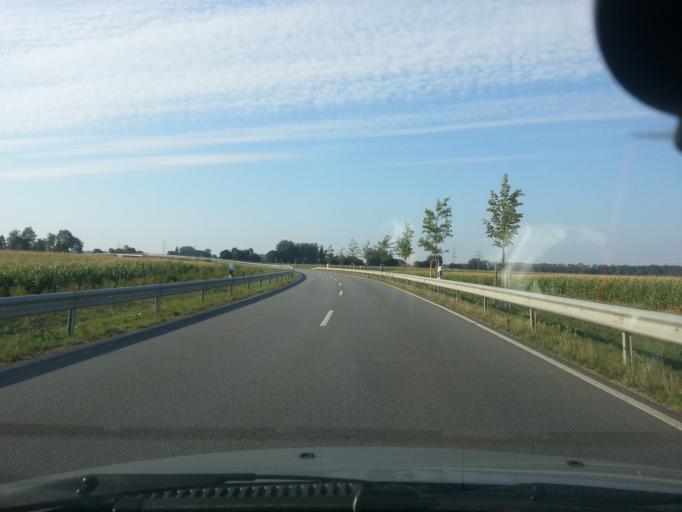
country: DE
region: Hesse
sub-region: Regierungsbezirk Darmstadt
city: Bensheim
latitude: 49.6845
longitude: 8.5852
